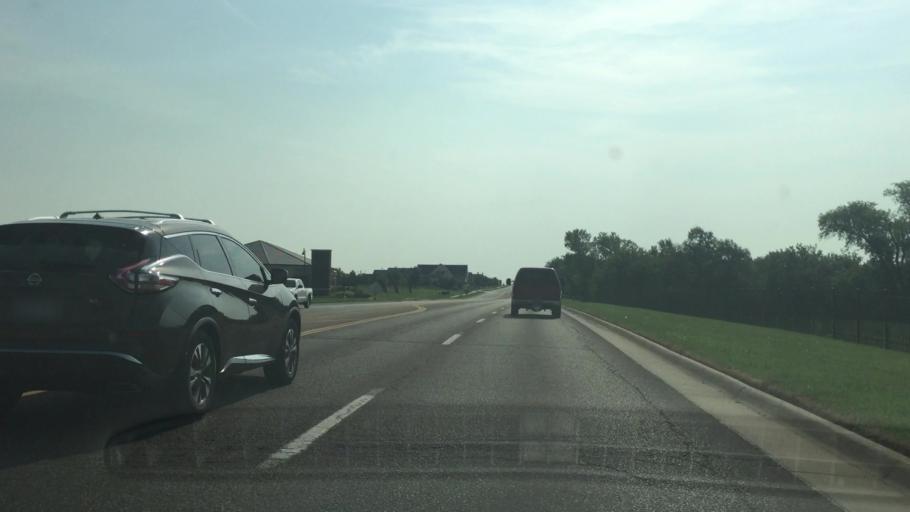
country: US
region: Kansas
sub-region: Sedgwick County
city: Bellaire
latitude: 37.7084
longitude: -97.2199
